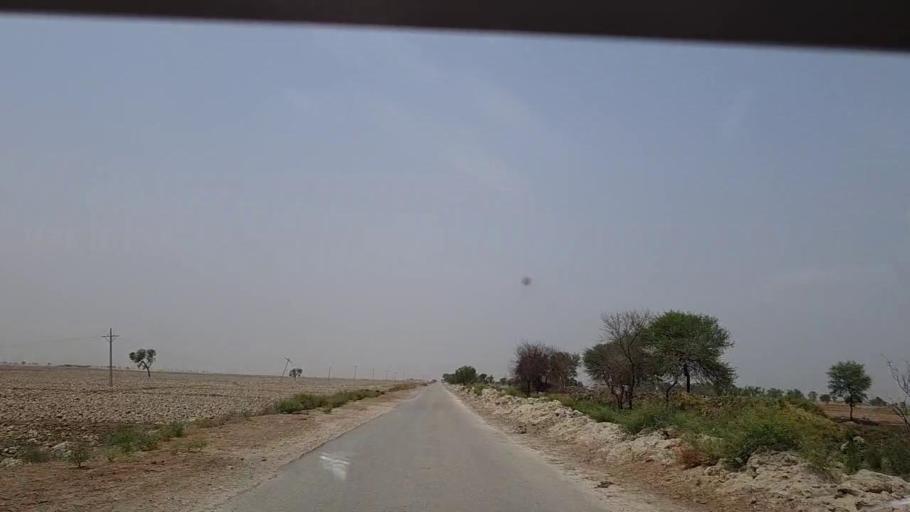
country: PK
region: Sindh
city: Khairpur Nathan Shah
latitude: 27.0243
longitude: 67.6210
